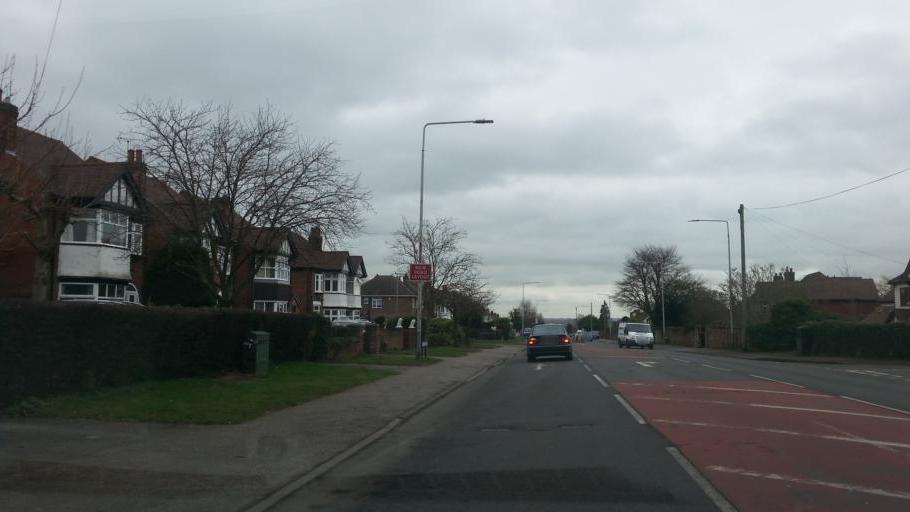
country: GB
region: England
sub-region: Nottinghamshire
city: Kimberley
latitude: 52.9942
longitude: -1.2456
